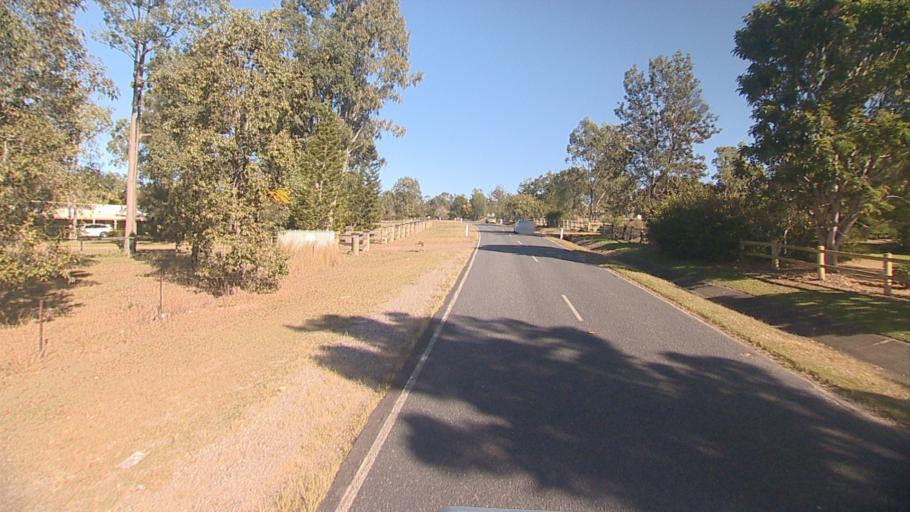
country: AU
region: Queensland
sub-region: Logan
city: North Maclean
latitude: -27.8199
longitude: 152.9601
